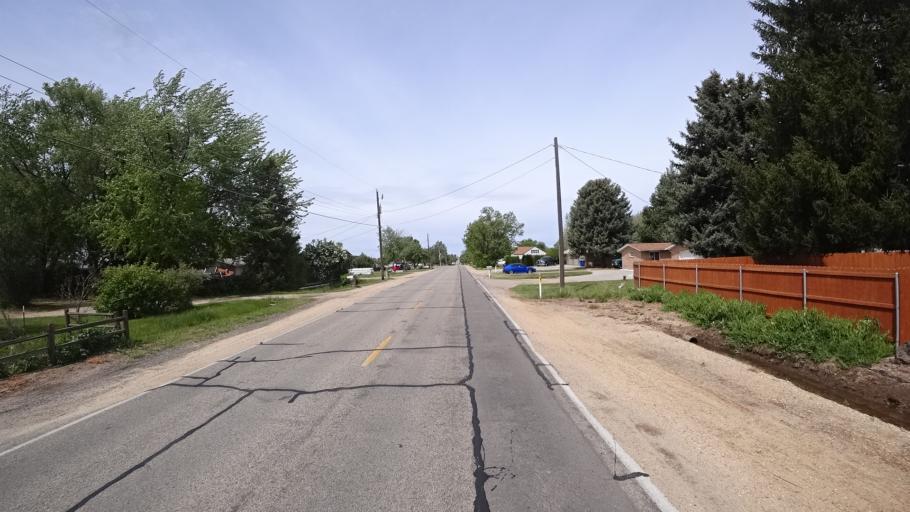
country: US
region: Idaho
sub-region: Ada County
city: Meridian
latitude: 43.5612
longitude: -116.3170
